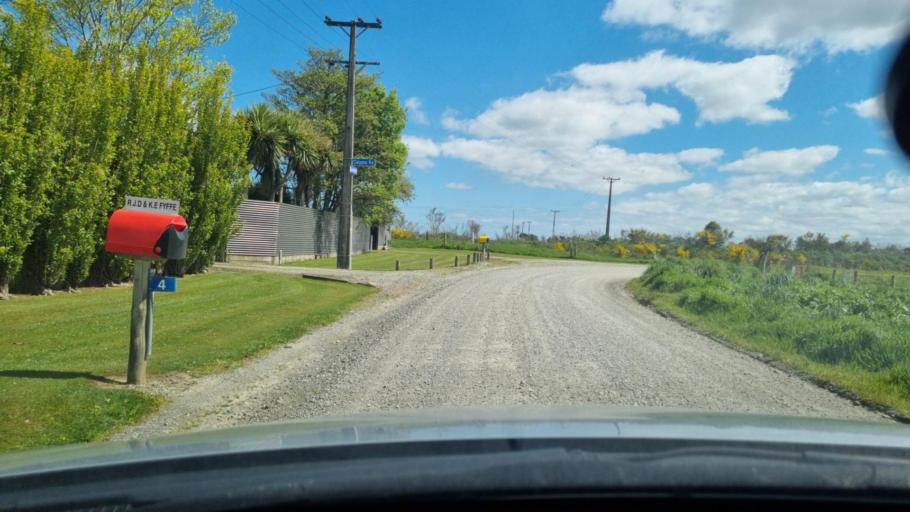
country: NZ
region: Southland
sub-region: Invercargill City
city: Invercargill
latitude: -46.3366
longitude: 168.3412
